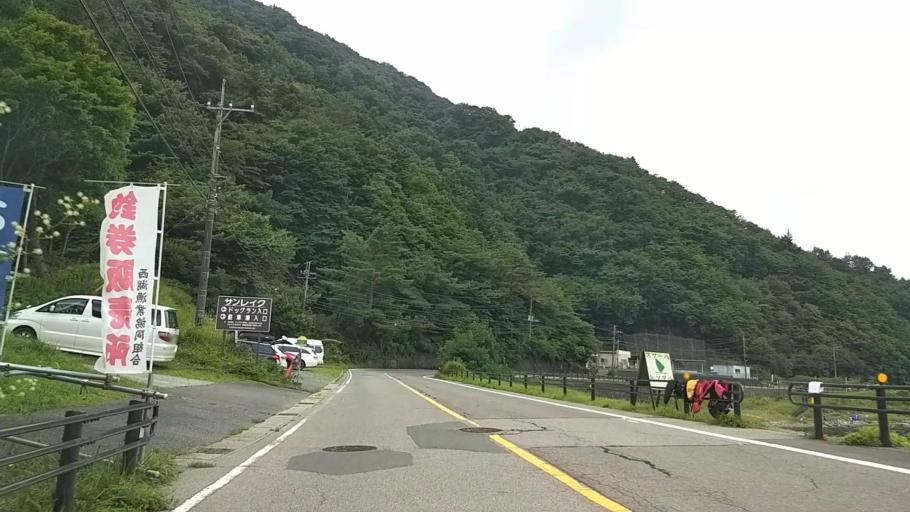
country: JP
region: Yamanashi
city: Fujikawaguchiko
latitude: 35.4965
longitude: 138.6927
